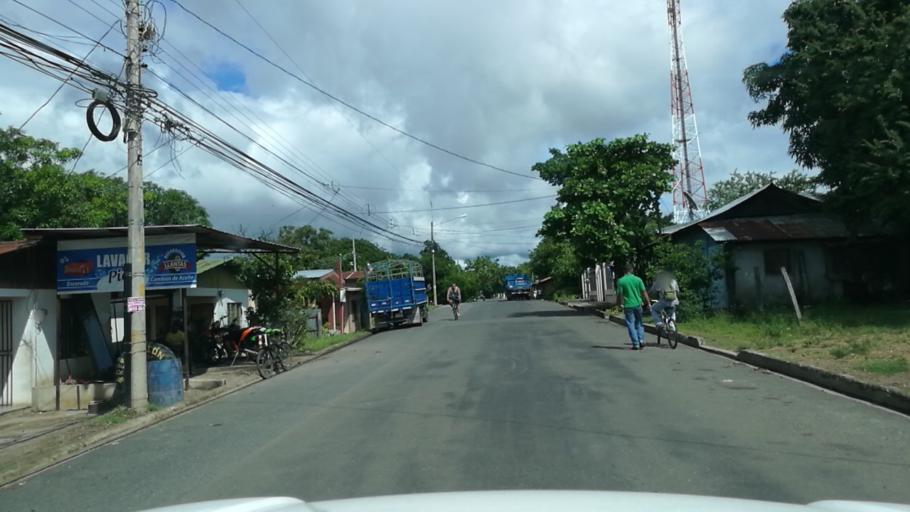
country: CR
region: Guanacaste
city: Bagaces
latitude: 10.5296
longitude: -85.2545
